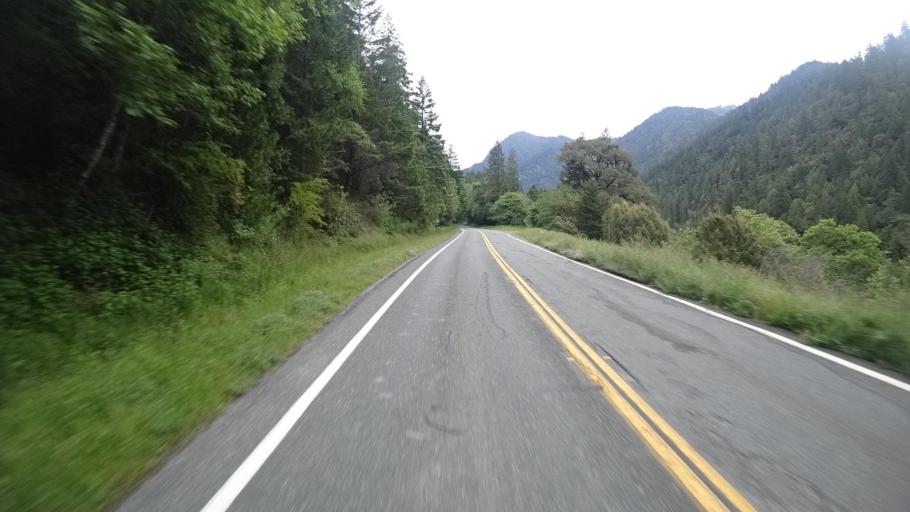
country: US
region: California
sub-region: Humboldt County
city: Willow Creek
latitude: 41.2056
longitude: -123.6626
